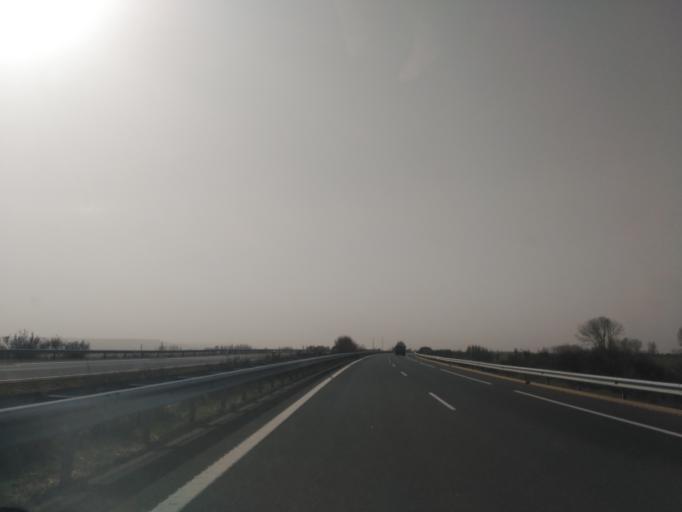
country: ES
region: Castille and Leon
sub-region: Provincia de Palencia
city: Pina de Campos
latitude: 42.2279
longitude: -4.4311
